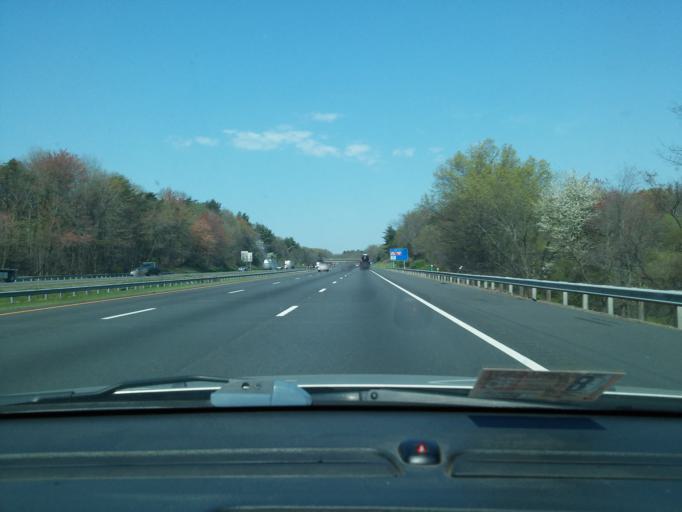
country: US
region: New Jersey
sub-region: Hunterdon County
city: Whitehouse Station
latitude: 40.6478
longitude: -74.7339
